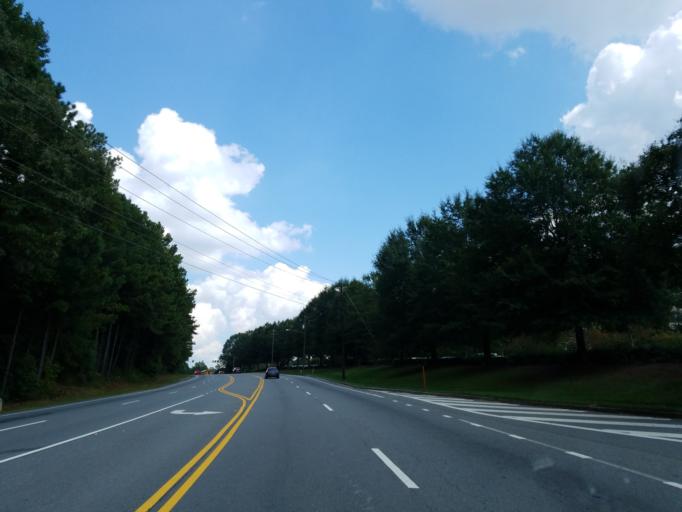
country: US
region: Georgia
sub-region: Fulton County
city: Alpharetta
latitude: 34.0590
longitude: -84.2921
